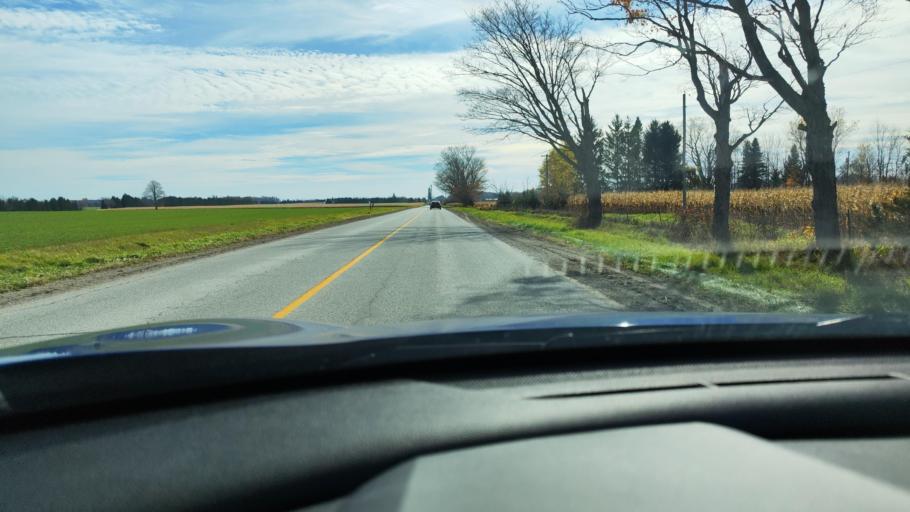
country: CA
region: Ontario
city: Wasaga Beach
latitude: 44.4518
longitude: -80.0013
